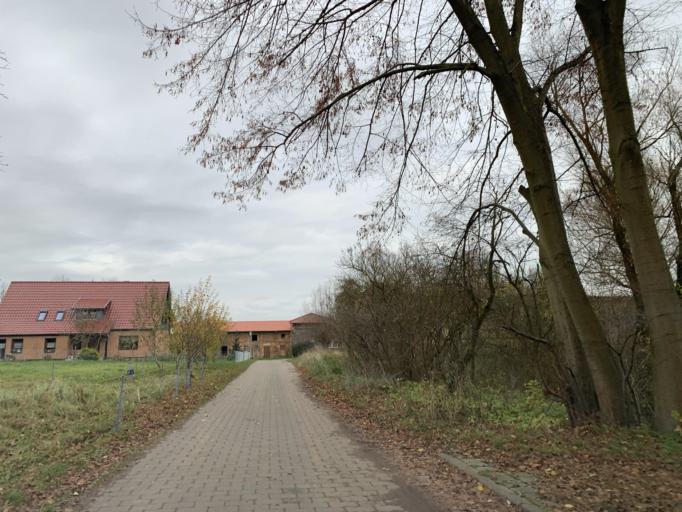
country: DE
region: Mecklenburg-Vorpommern
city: Carpin
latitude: 53.4049
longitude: 13.2001
